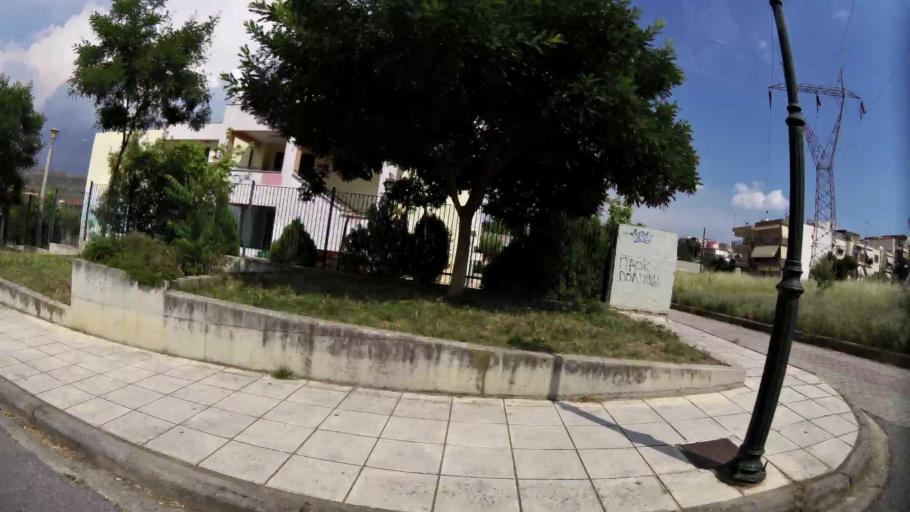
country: GR
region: Central Macedonia
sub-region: Nomos Thessalonikis
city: Polichni
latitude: 40.6662
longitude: 22.9510
